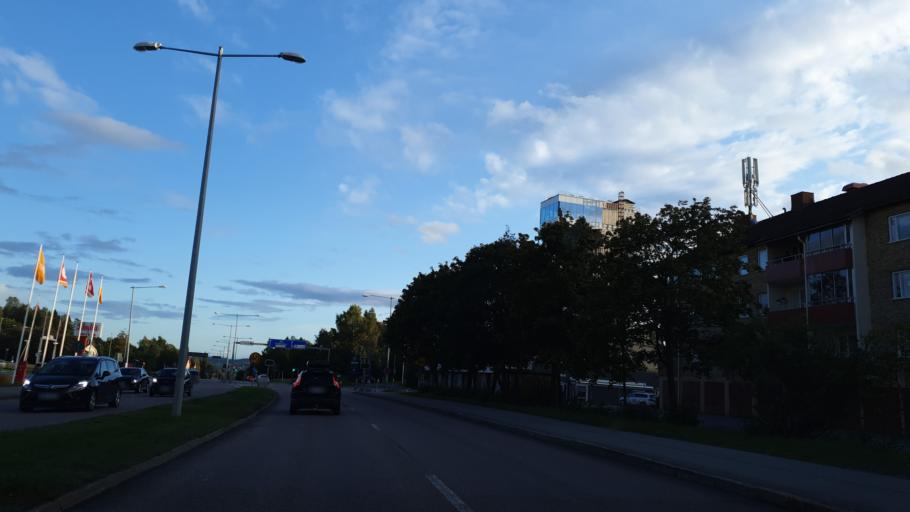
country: SE
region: Vaesternorrland
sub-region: OErnskoeldsviks Kommun
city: Ornskoldsvik
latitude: 63.2971
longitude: 18.7185
